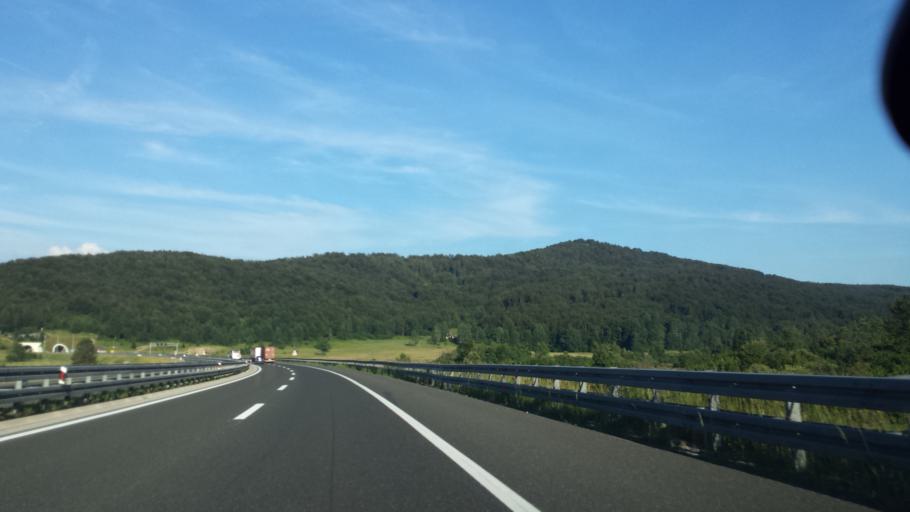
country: HR
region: Primorsko-Goranska
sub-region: Grad Delnice
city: Delnice
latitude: 45.3814
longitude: 14.8468
